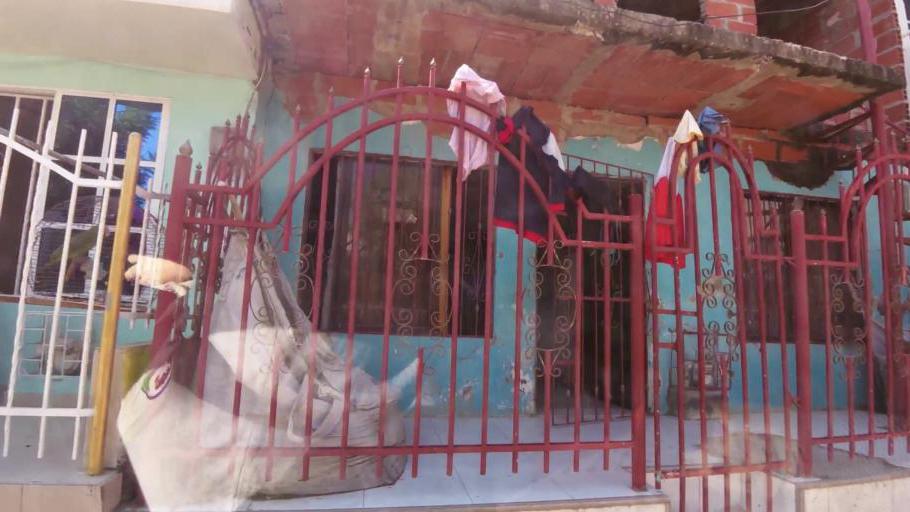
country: CO
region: Bolivar
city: Cartagena
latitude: 10.3859
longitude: -75.5073
